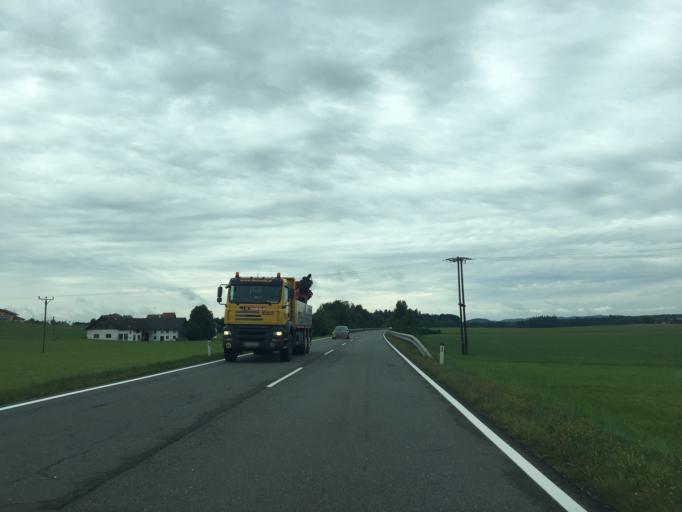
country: AT
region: Salzburg
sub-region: Politischer Bezirk Salzburg-Umgebung
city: Lamprechtshausen
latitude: 48.0085
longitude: 12.9637
